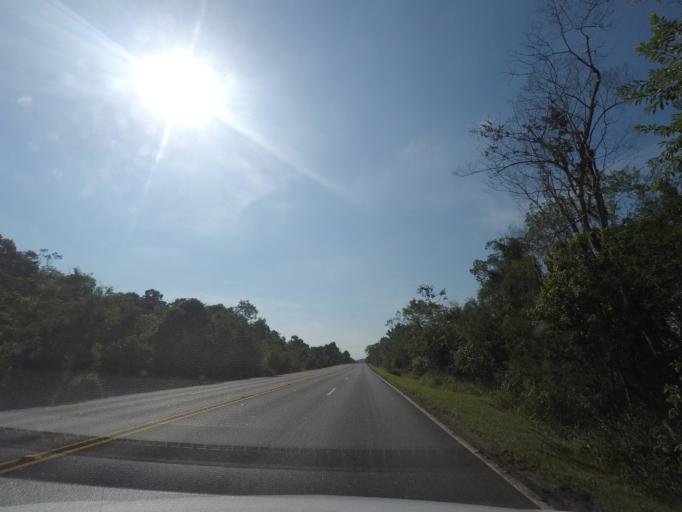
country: BR
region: Parana
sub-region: Paranagua
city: Paranagua
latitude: -25.5923
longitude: -48.6110
